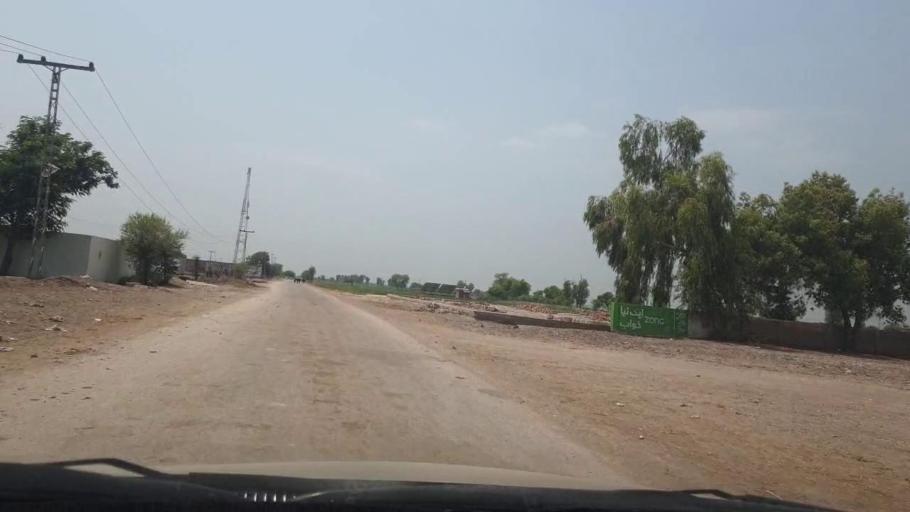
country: PK
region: Sindh
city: Ratodero
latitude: 27.7218
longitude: 68.2800
